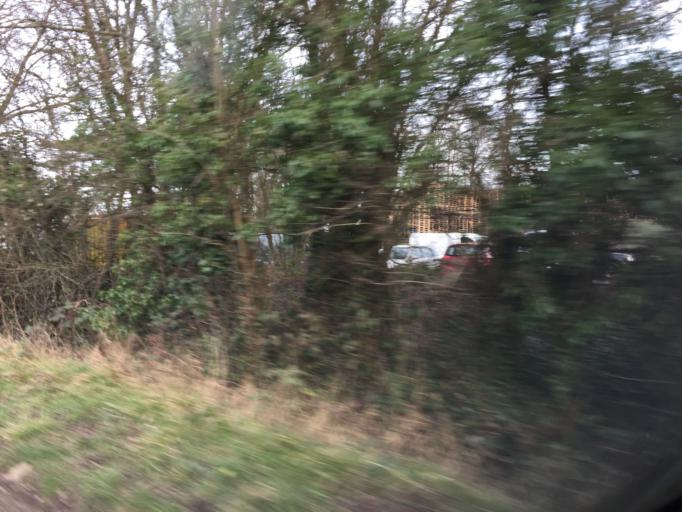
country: GB
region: England
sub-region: South Gloucestershire
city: Yate
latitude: 51.5709
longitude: -2.4254
